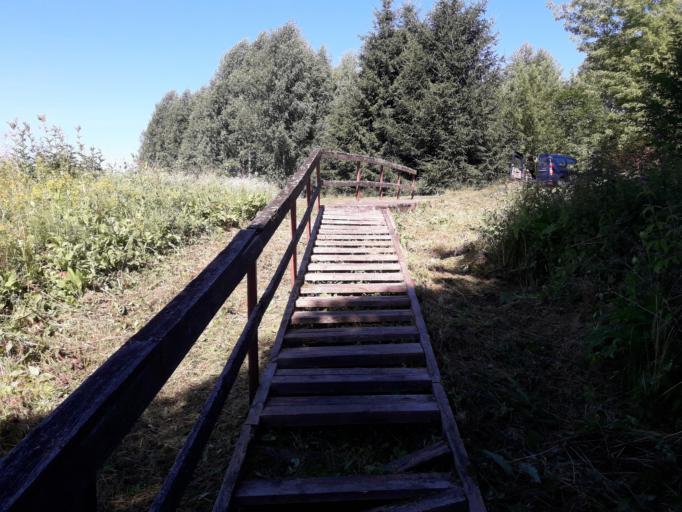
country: LT
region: Alytaus apskritis
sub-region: Alytaus rajonas
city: Daugai
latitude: 54.1169
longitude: 24.3022
